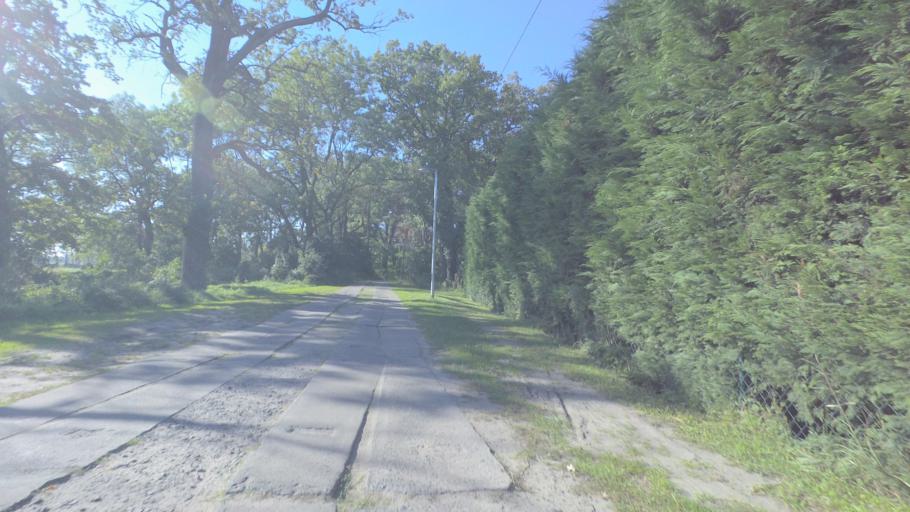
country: DE
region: Brandenburg
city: Rangsdorf
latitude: 52.3034
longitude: 13.3769
